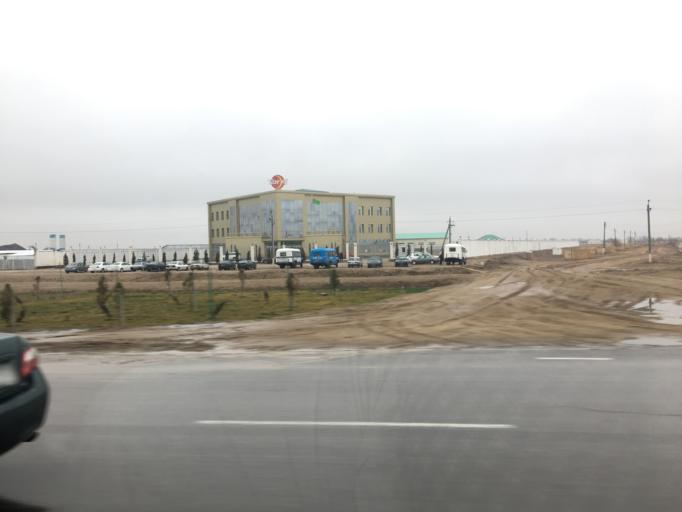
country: TM
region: Mary
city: Mary
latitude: 37.5499
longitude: 61.7483
